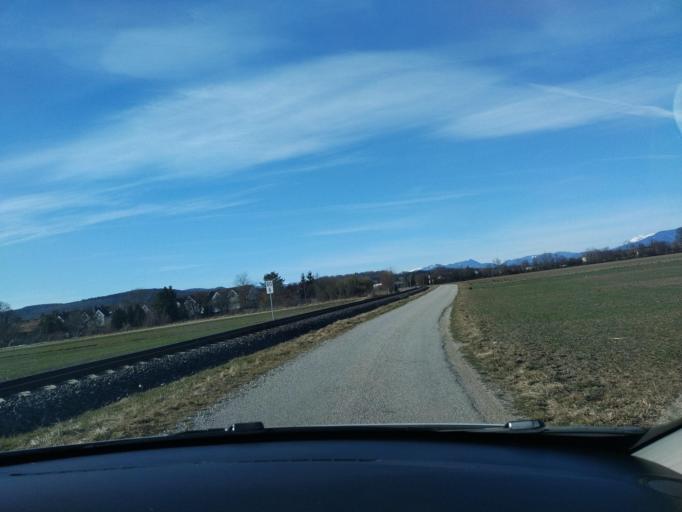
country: AT
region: Lower Austria
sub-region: Politischer Bezirk Wiener Neustadt
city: Bad Erlach
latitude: 47.7394
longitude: 16.2201
